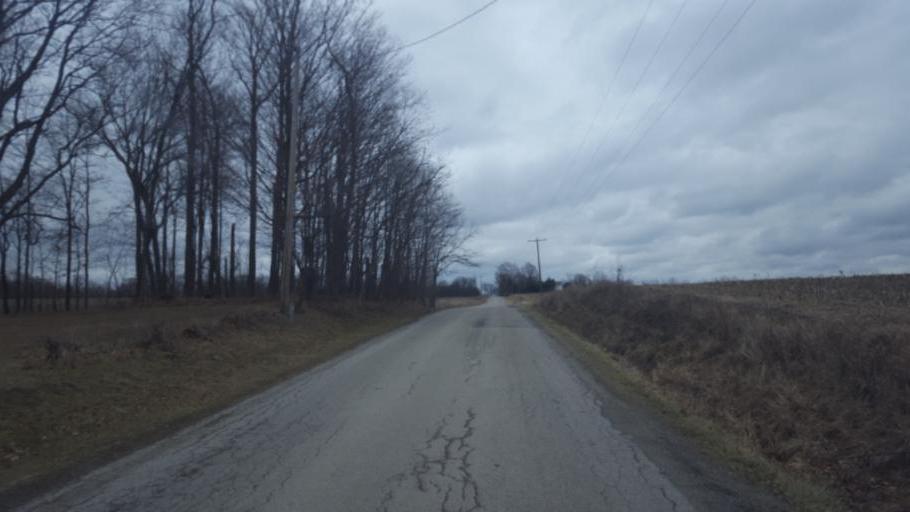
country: US
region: Ohio
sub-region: Morrow County
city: Mount Gilead
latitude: 40.6398
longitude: -82.8456
